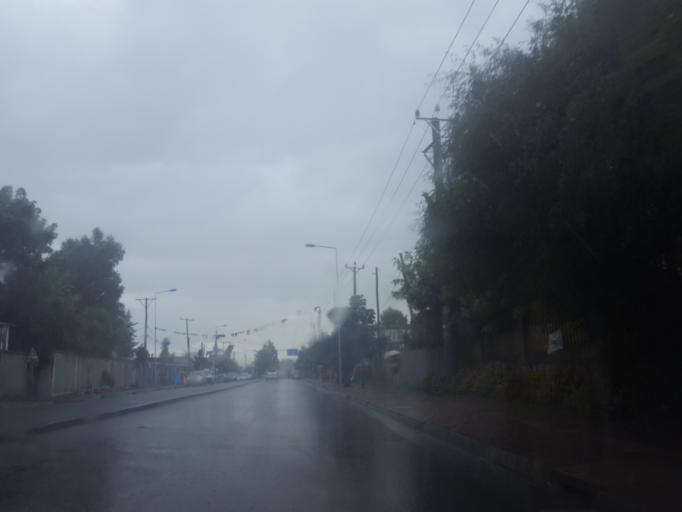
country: ET
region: Adis Abeba
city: Addis Ababa
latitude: 9.0276
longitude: 38.7779
